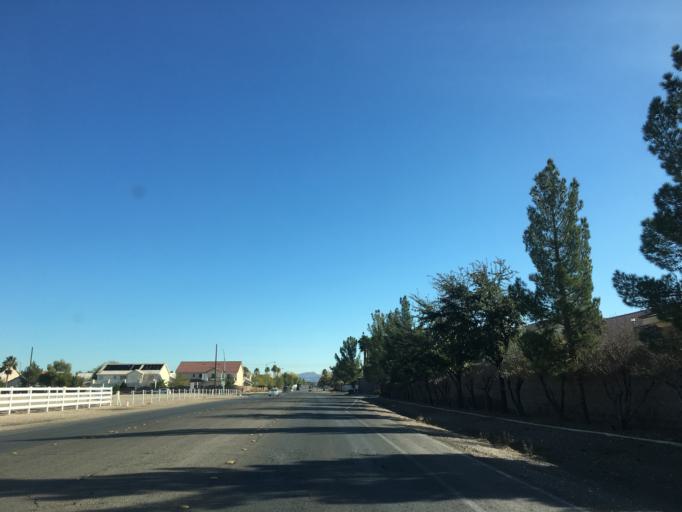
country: US
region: Nevada
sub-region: Clark County
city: Enterprise
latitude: 36.0065
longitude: -115.1653
